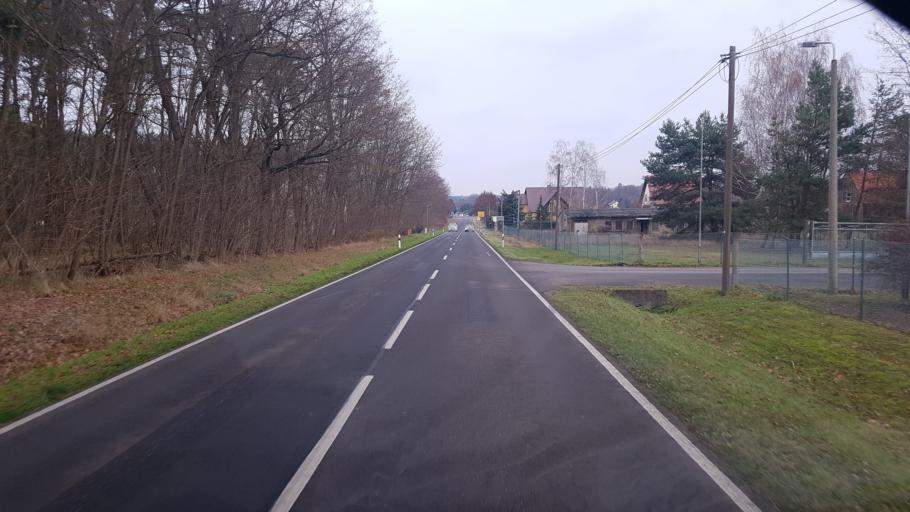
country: DE
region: Brandenburg
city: Schenkendobern
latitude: 51.9490
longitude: 14.6355
